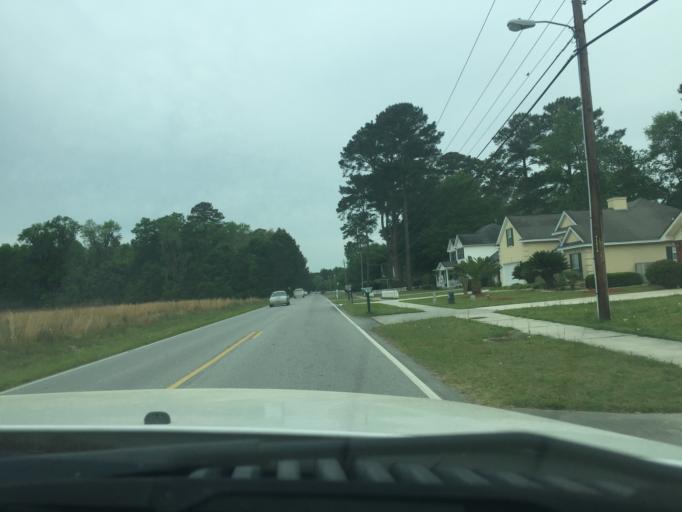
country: US
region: Georgia
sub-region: Chatham County
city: Georgetown
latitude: 31.9693
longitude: -81.2350
